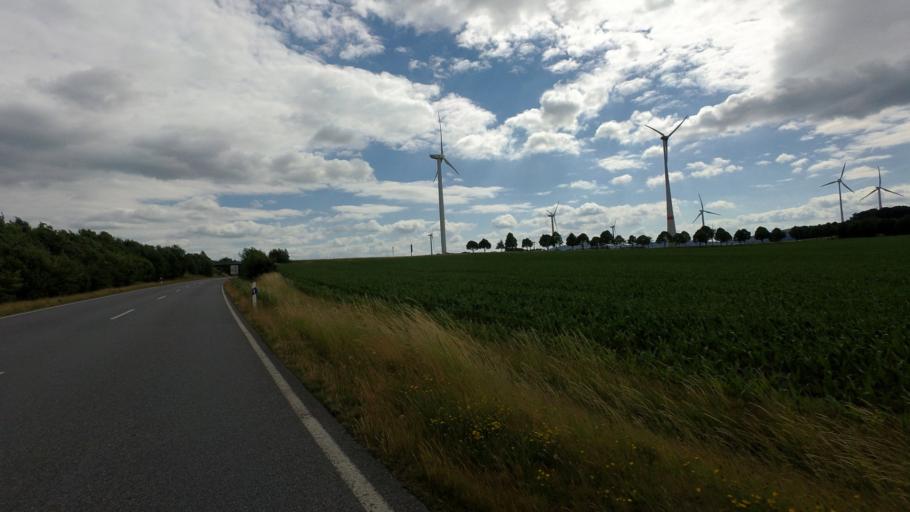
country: DE
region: Saxony
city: Nebelschutz
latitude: 51.2457
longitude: 14.1677
